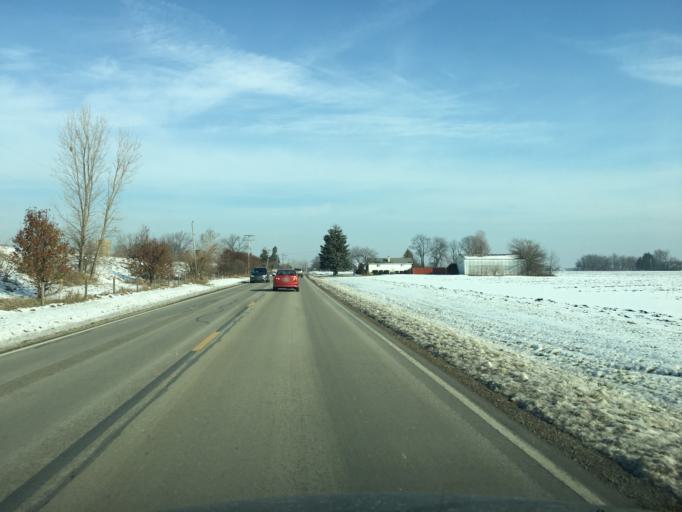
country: US
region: Illinois
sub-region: Will County
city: Plainfield
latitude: 41.6749
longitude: -88.1716
